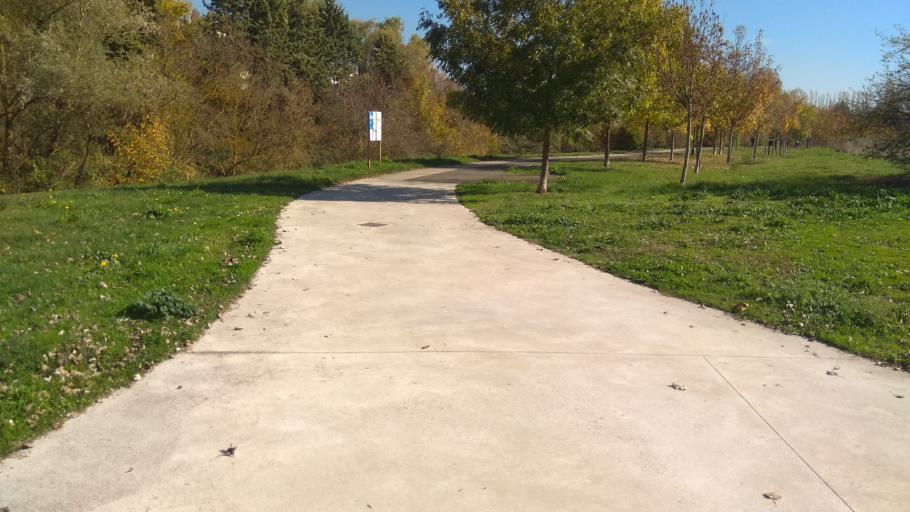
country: ES
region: Navarre
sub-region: Provincia de Navarra
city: Baranain
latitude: 42.8015
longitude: -1.6756
